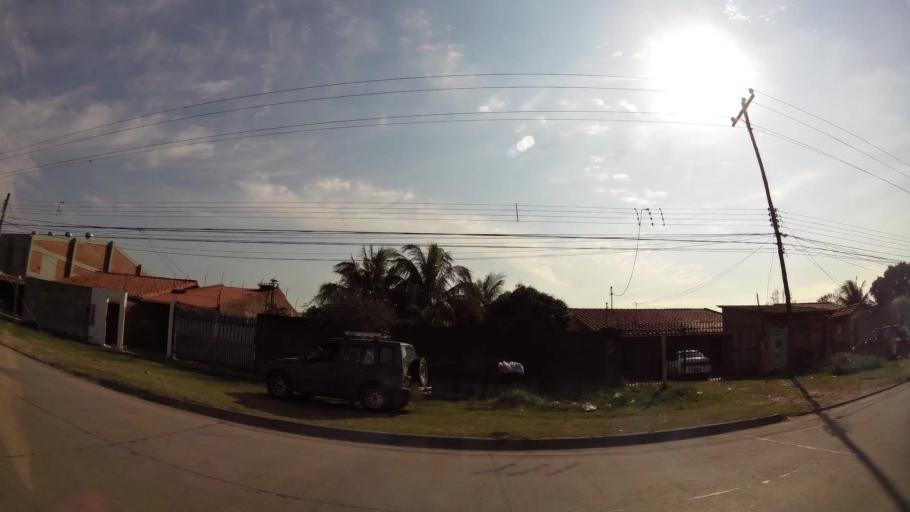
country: BO
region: Santa Cruz
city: Santa Cruz de la Sierra
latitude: -17.7361
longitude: -63.1569
